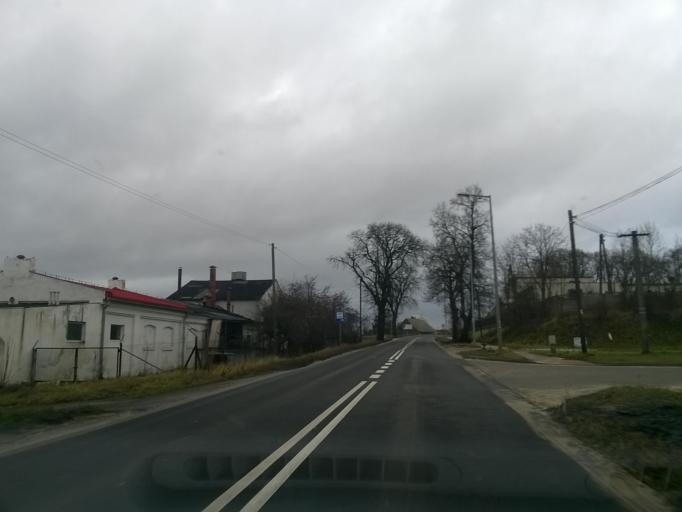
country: PL
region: Kujawsko-Pomorskie
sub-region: Powiat nakielski
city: Kcynia
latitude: 52.9904
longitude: 17.4783
